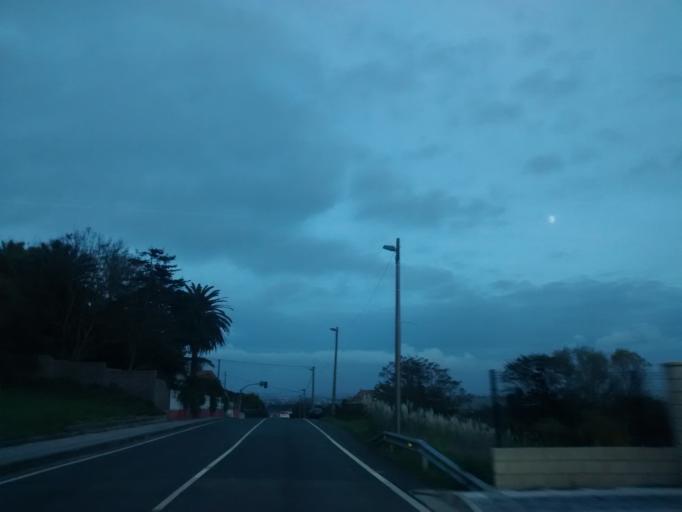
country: ES
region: Cantabria
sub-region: Provincia de Cantabria
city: Santa Cruz de Bezana
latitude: 43.4614
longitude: -3.9210
